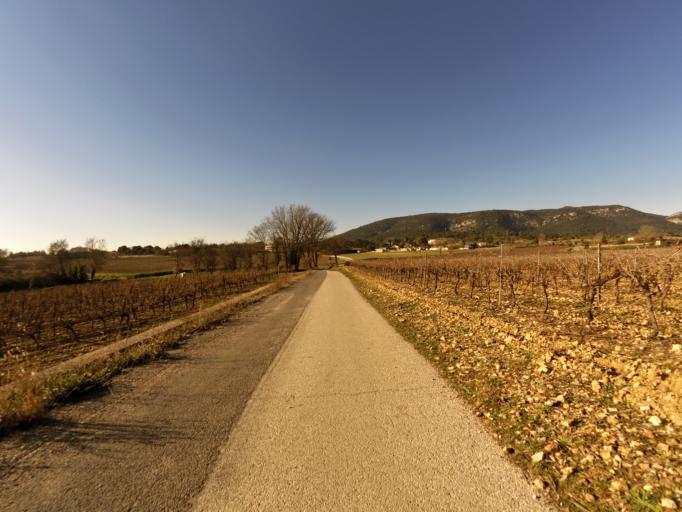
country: FR
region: Languedoc-Roussillon
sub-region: Departement du Gard
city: Quissac
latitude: 43.8938
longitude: 3.9957
